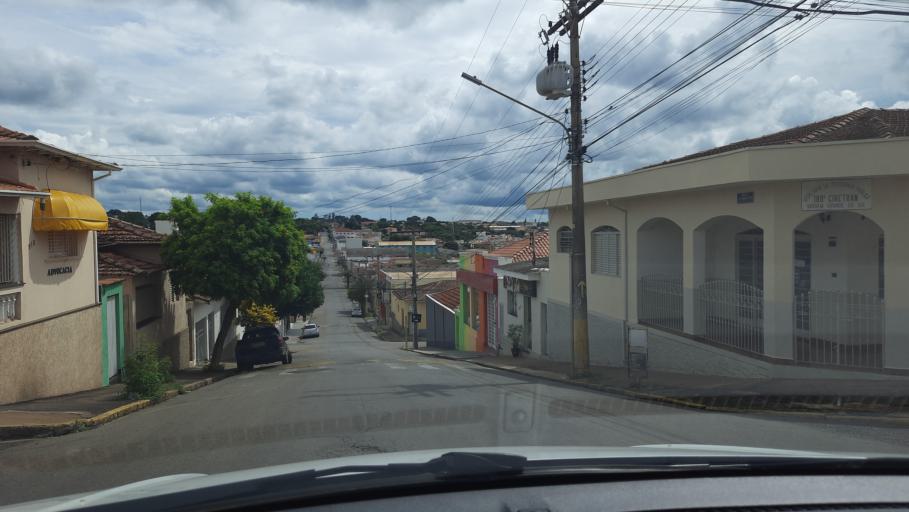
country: BR
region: Sao Paulo
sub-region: Vargem Grande Do Sul
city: Vargem Grande do Sul
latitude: -21.8325
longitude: -46.8949
